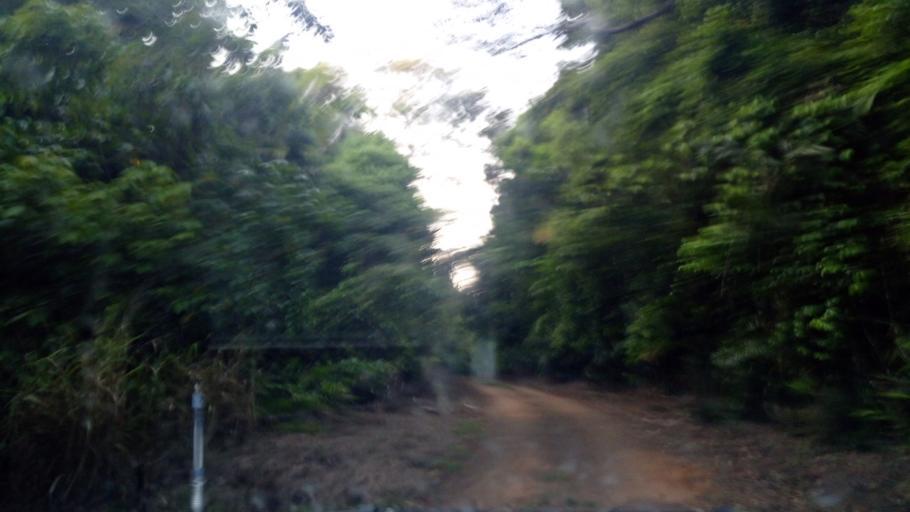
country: AU
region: Queensland
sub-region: Tablelands
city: Atherton
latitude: -17.3700
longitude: 145.7537
